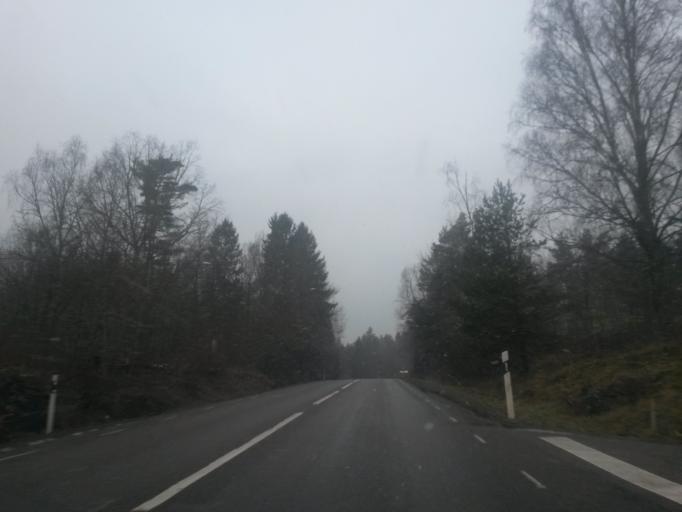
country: SE
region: Vaestra Goetaland
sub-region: Vanersborgs Kommun
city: Vargon
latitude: 58.2515
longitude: 12.4169
